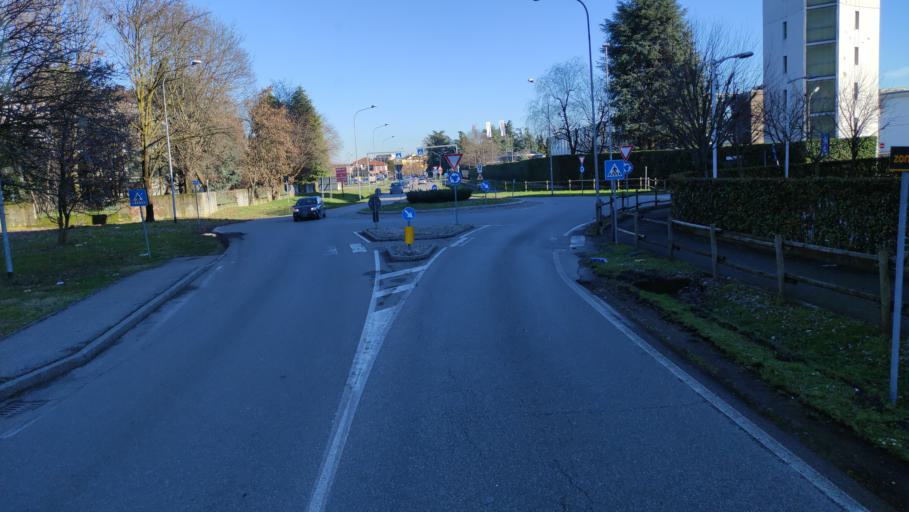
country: IT
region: Lombardy
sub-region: Provincia di Monza e Brianza
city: Concorezzo
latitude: 45.5903
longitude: 9.3266
